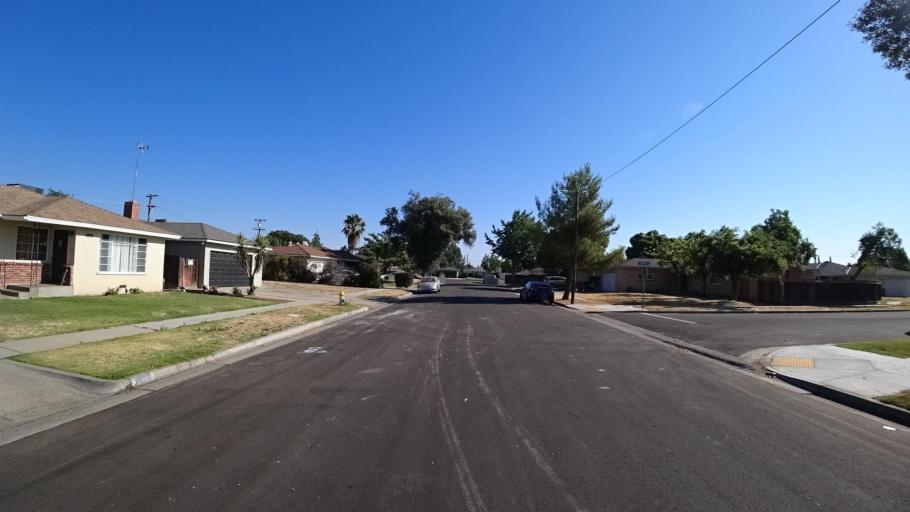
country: US
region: California
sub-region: Fresno County
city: Fresno
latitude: 36.7845
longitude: -119.7605
